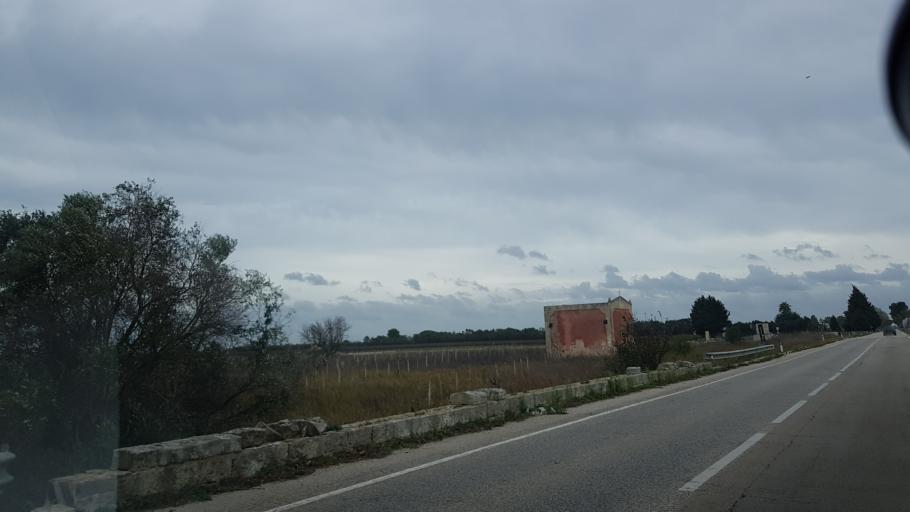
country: IT
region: Apulia
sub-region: Provincia di Brindisi
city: San Pancrazio Salentino
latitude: 40.4140
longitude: 17.8561
